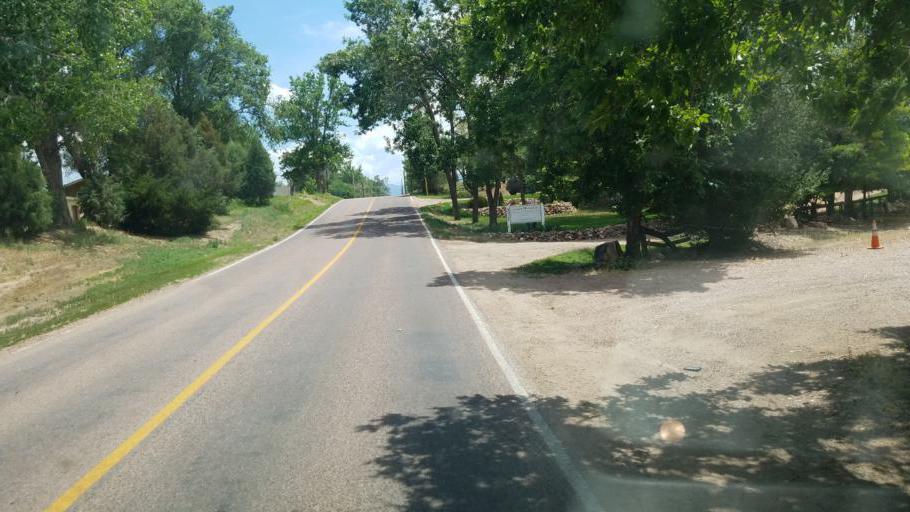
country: US
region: Colorado
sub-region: Fremont County
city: Lincoln Park
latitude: 38.4246
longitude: -105.1995
